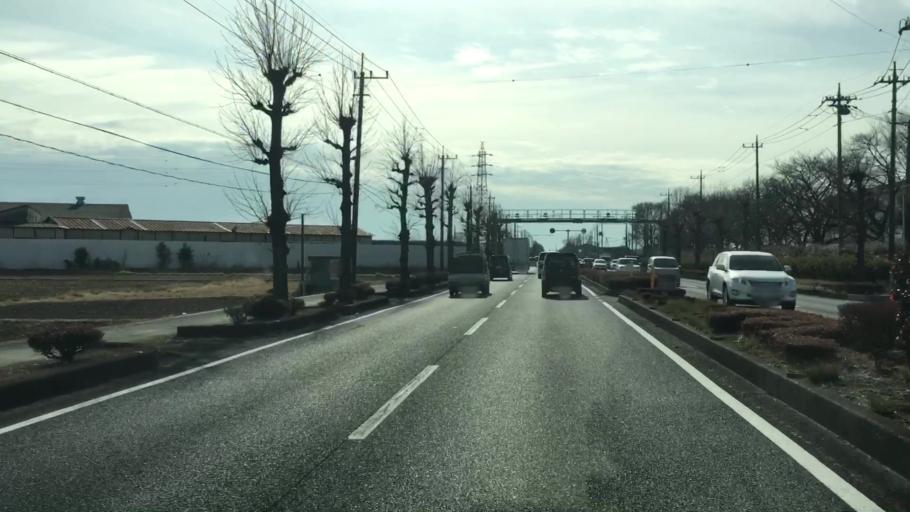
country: JP
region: Saitama
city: Menuma
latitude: 36.2018
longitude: 139.3706
